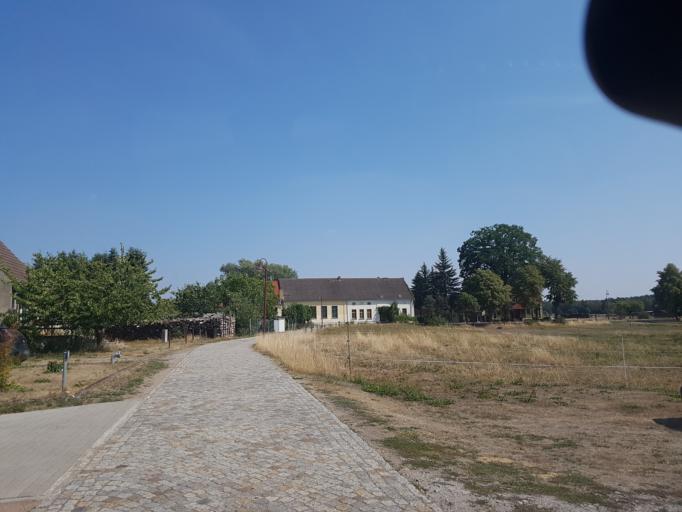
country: DE
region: Brandenburg
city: Wiesenburg
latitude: 52.0701
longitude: 12.3830
